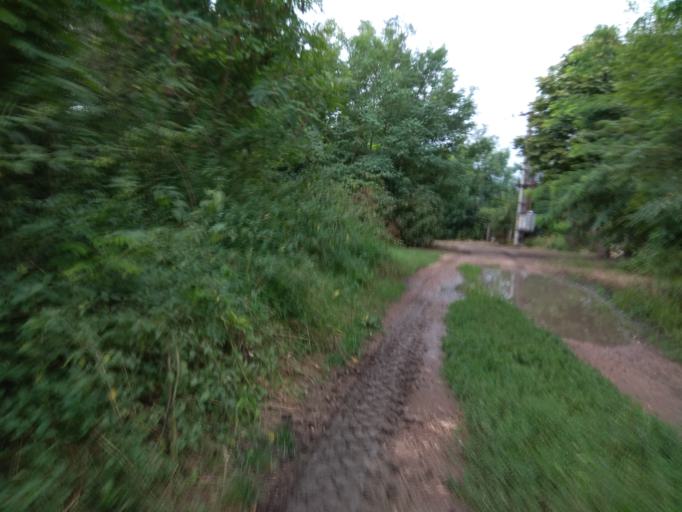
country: HU
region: Borsod-Abauj-Zemplen
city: Monok
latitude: 48.1758
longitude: 21.1212
